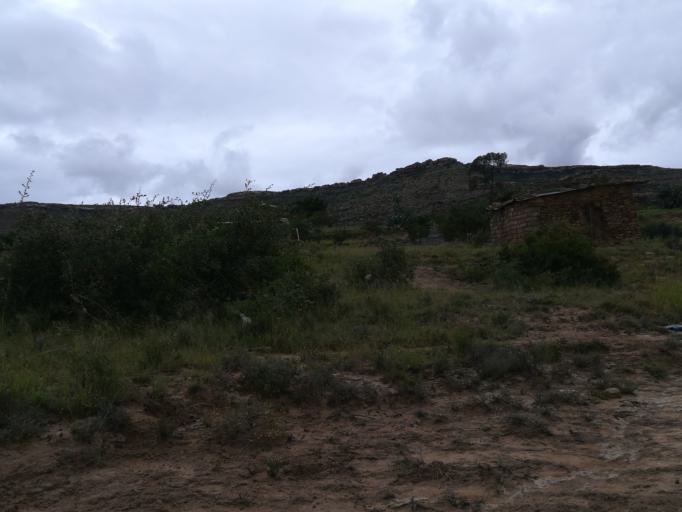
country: LS
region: Quthing
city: Quthing
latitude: -30.3353
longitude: 27.5315
